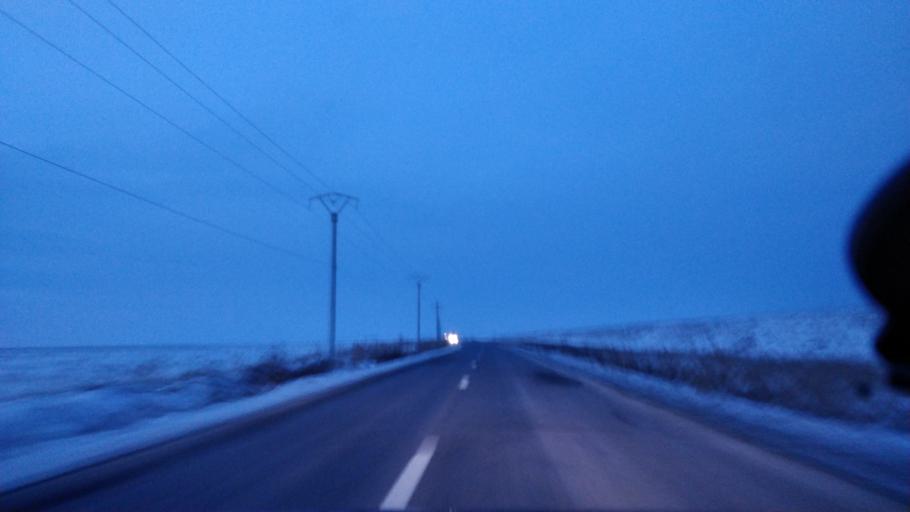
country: RO
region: Vrancea
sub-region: Comuna Nanesti
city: Nanesti
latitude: 45.5616
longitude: 27.4997
